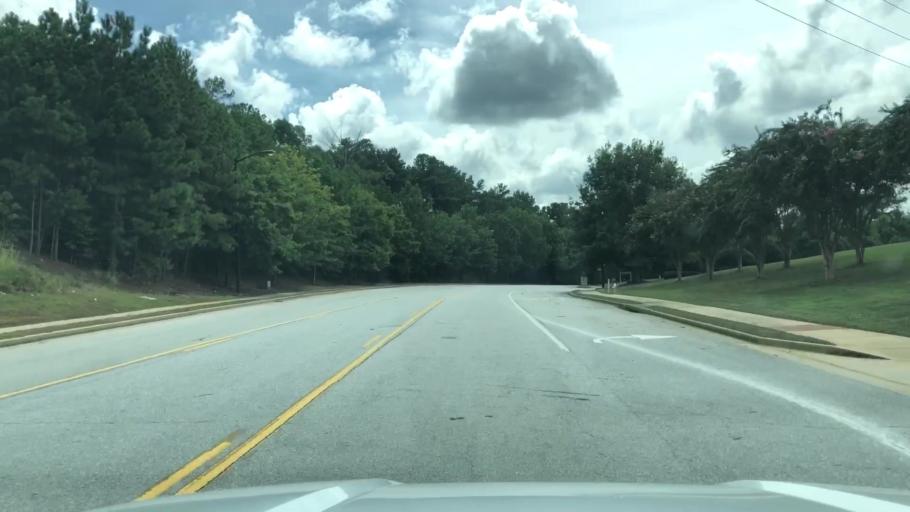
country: US
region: Georgia
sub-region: Gwinnett County
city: Suwanee
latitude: 34.0382
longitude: -84.0313
